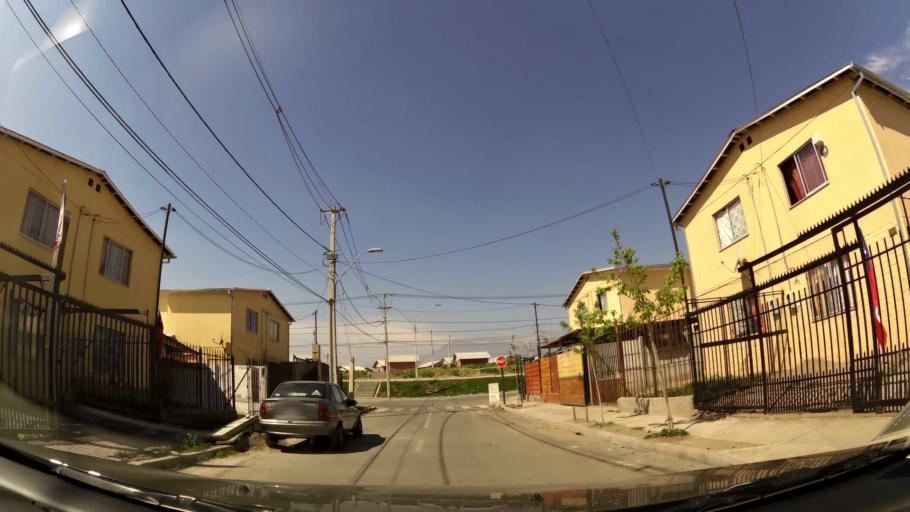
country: CL
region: Santiago Metropolitan
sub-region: Provincia de Cordillera
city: Puente Alto
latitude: -33.6301
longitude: -70.6067
